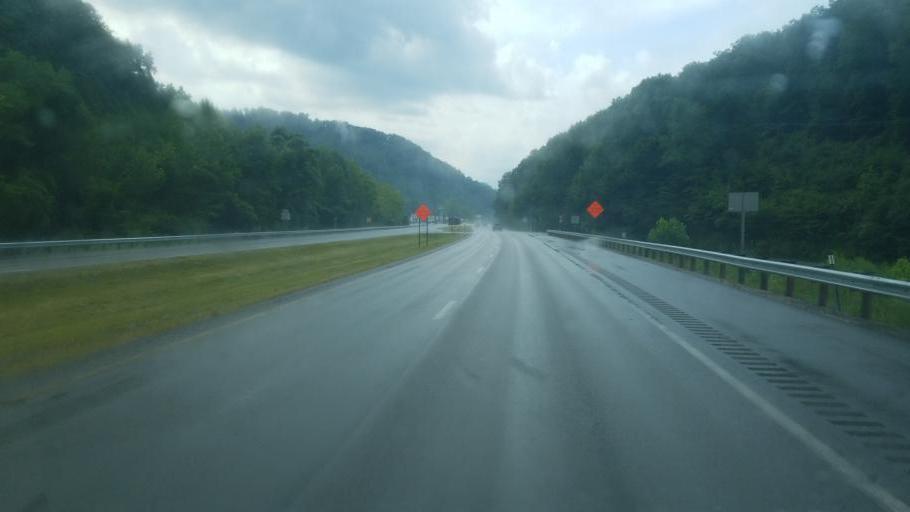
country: US
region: West Virginia
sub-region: Logan County
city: Chapmanville
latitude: 37.9866
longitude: -81.9640
